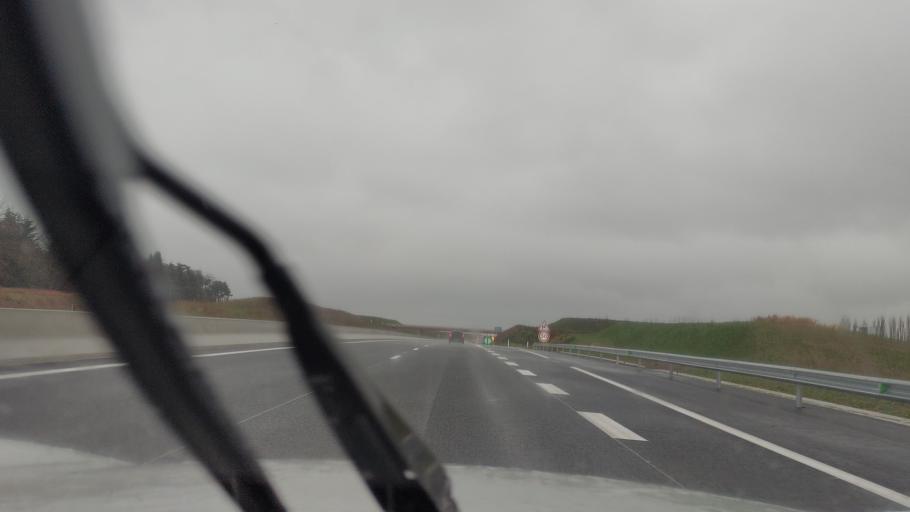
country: FR
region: Ile-de-France
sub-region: Departement de Seine-et-Marne
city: Mitry-Mory
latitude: 49.0129
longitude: 2.5962
